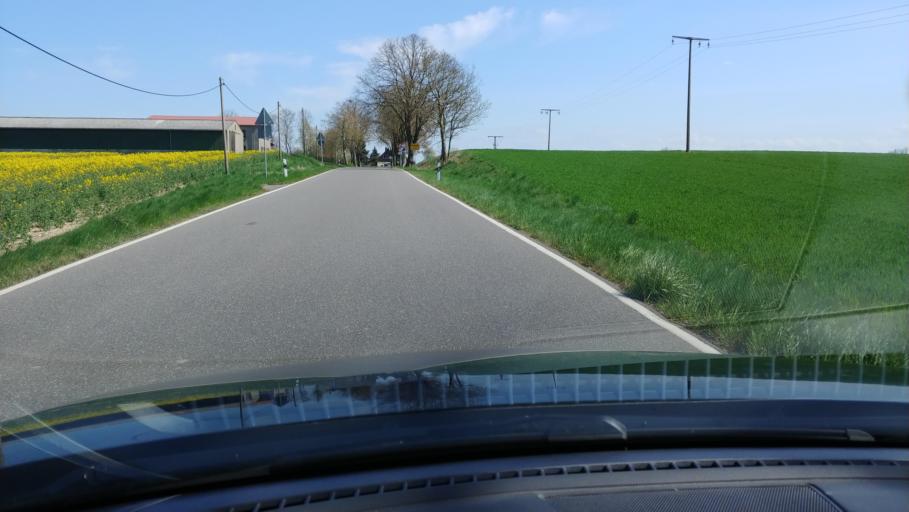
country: DE
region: Mecklenburg-Vorpommern
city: Muhlen Eichsen
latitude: 53.7965
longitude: 11.2852
